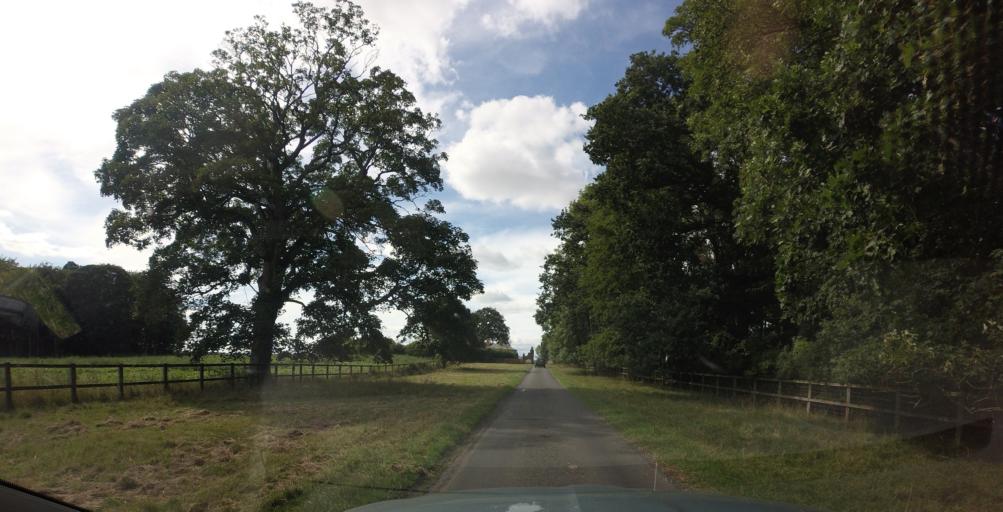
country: GB
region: England
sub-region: North Yorkshire
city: Ripon
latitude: 54.1094
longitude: -1.4732
